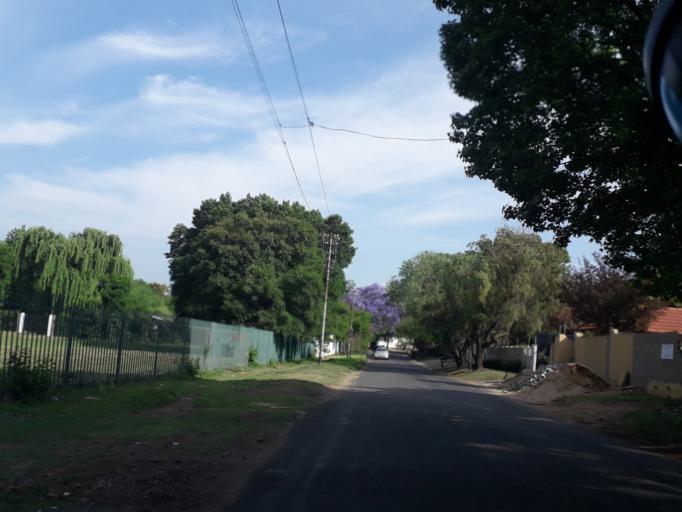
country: ZA
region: Gauteng
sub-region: City of Johannesburg Metropolitan Municipality
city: Johannesburg
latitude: -26.1532
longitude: 28.0259
